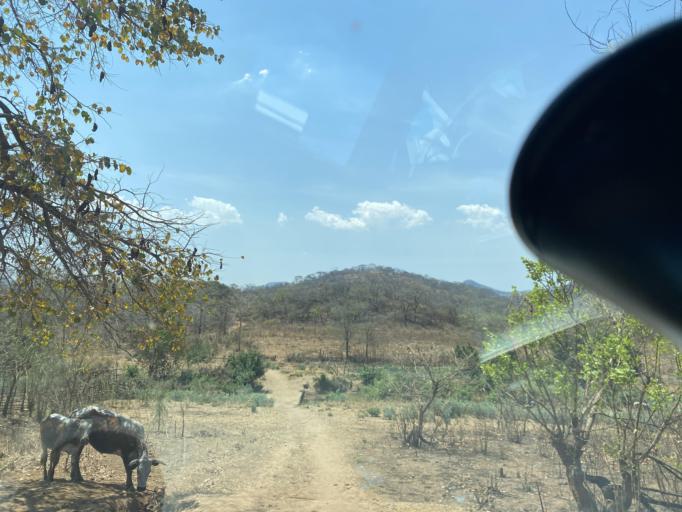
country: ZM
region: Lusaka
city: Kafue
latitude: -15.7865
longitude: 28.4607
